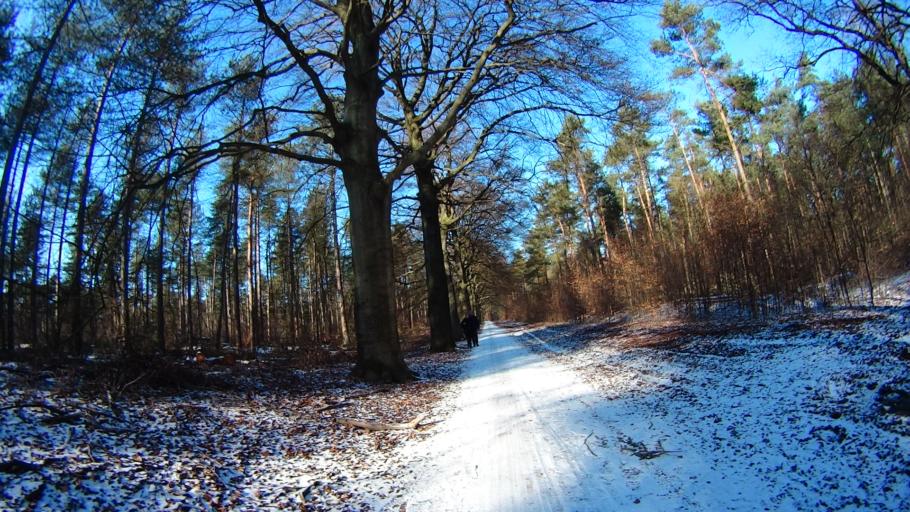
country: NL
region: North Holland
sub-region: Gemeente Hilversum
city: Hilversum
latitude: 52.1896
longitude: 5.2153
